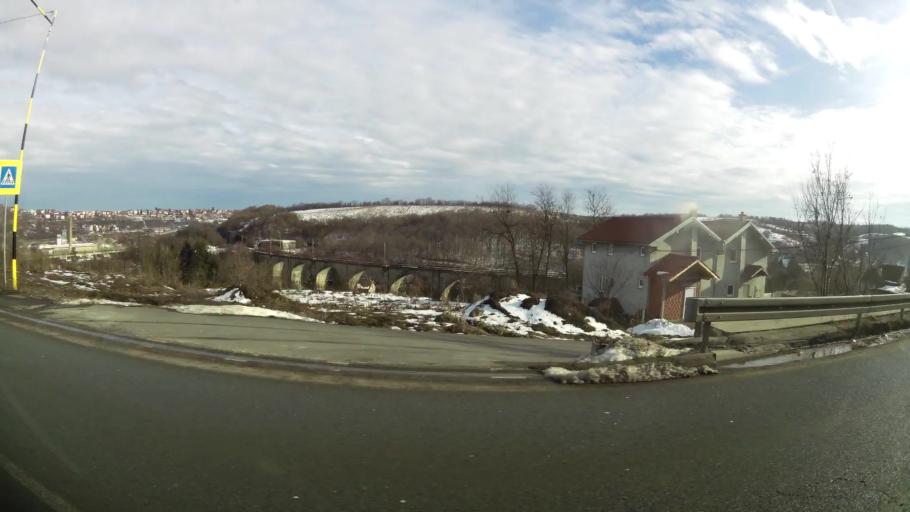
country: RS
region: Central Serbia
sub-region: Belgrade
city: Rakovica
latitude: 44.7200
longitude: 20.4321
